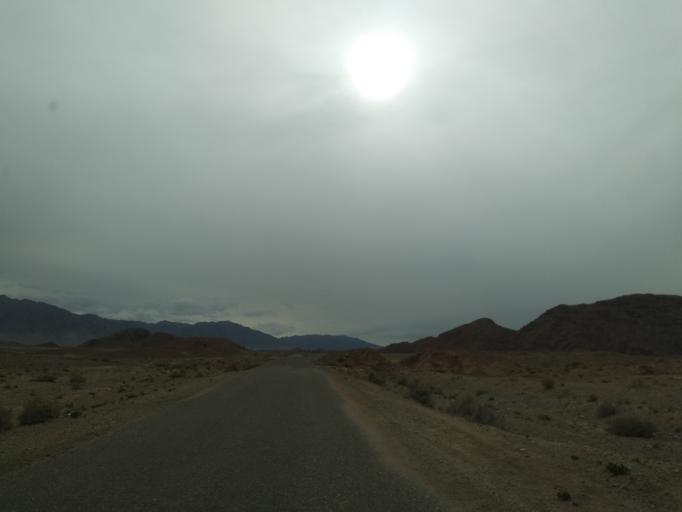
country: KG
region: Ysyk-Koel
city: Balykchy
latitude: 42.3151
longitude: 76.1526
